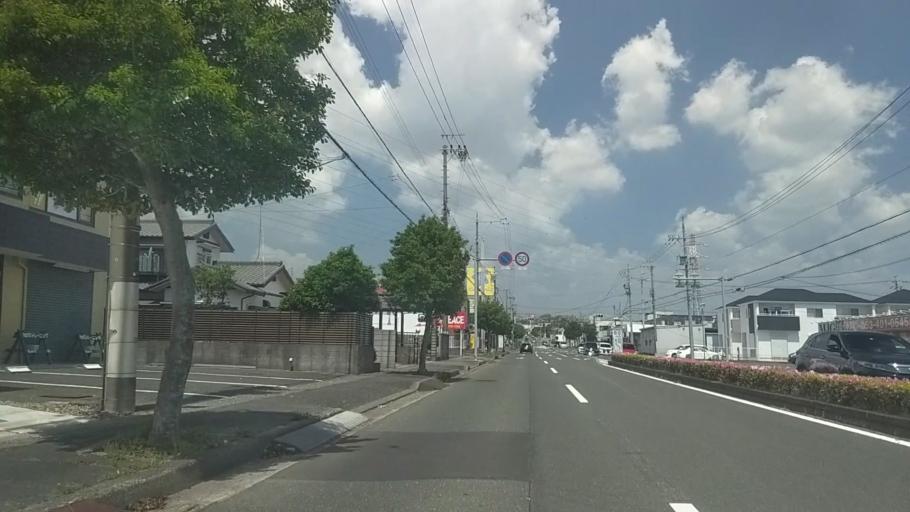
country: JP
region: Shizuoka
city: Hamamatsu
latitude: 34.7483
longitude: 137.7379
